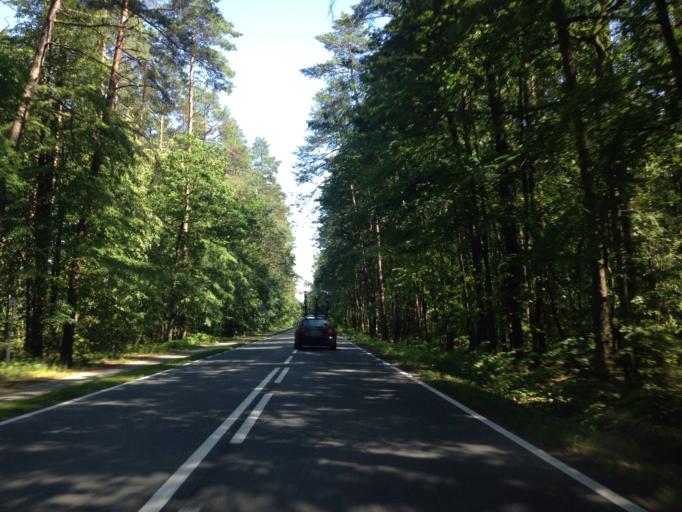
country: PL
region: Kujawsko-Pomorskie
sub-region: Powiat swiecki
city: Osie
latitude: 53.6135
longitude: 18.2874
